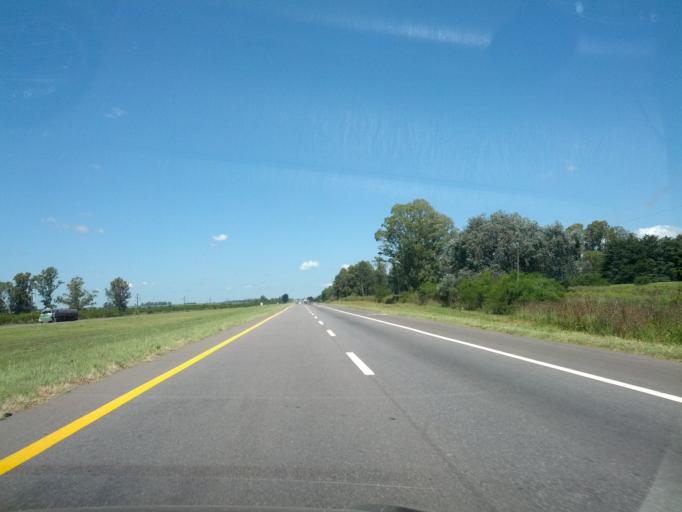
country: AR
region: Entre Rios
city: Gualeguaychu
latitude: -33.1317
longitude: -58.6571
